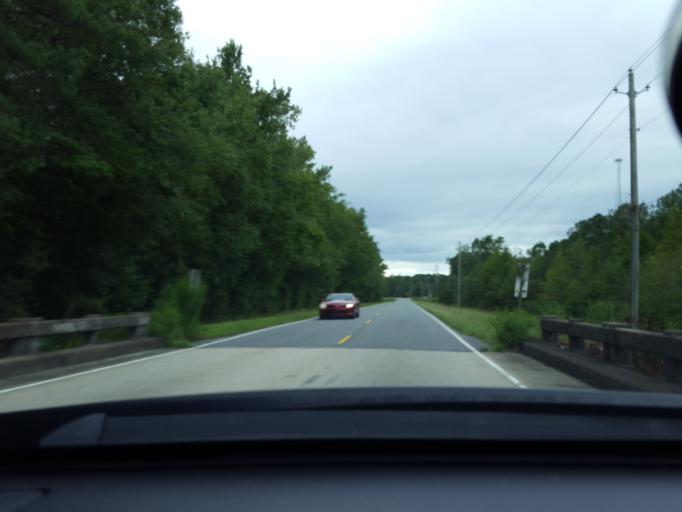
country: US
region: North Carolina
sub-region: Sampson County
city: Roseboro
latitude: 34.7595
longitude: -78.4117
